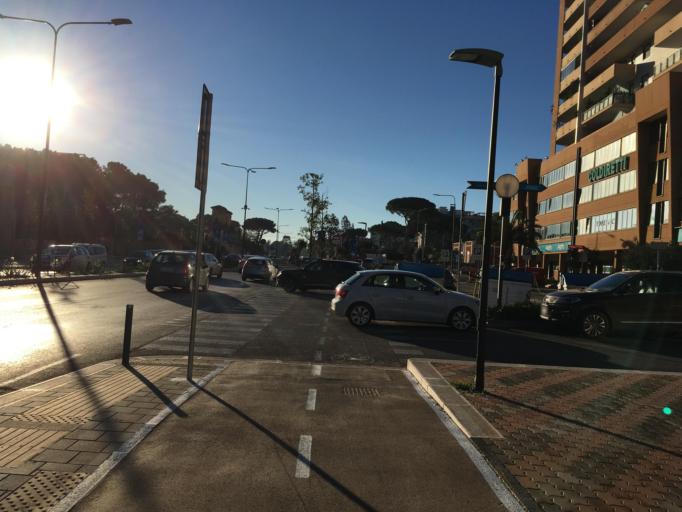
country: IT
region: Apulia
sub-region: Provincia di Bari
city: Bari
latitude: 41.1012
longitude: 16.8881
